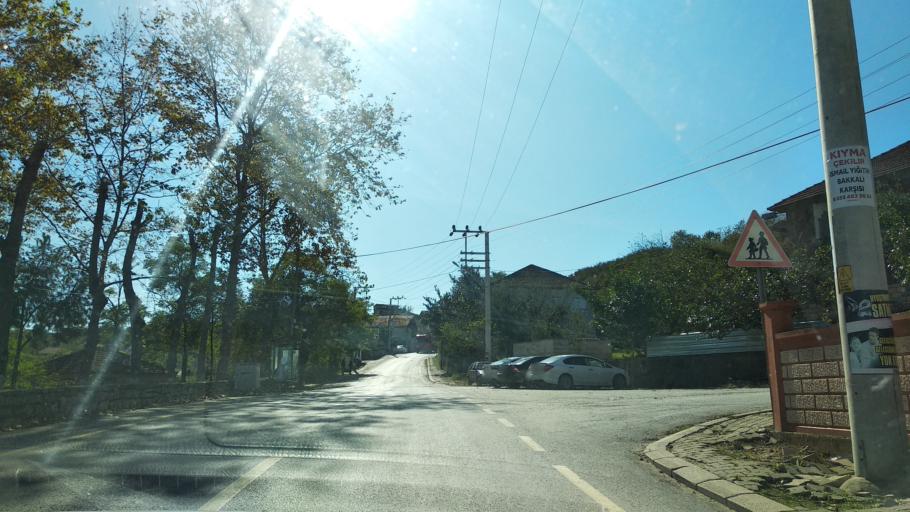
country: TR
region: Sakarya
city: Karasu
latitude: 41.1042
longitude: 30.6353
